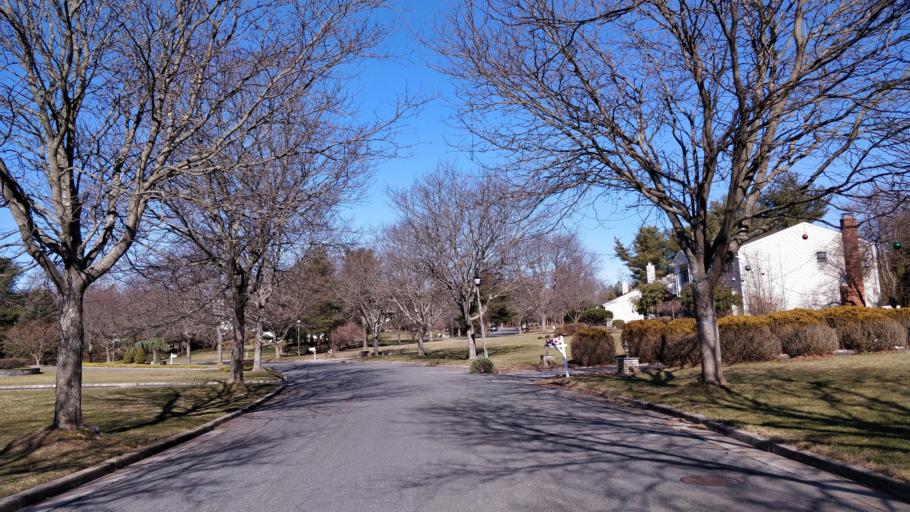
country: US
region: New York
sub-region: Suffolk County
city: Saint James
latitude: 40.8917
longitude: -73.1386
